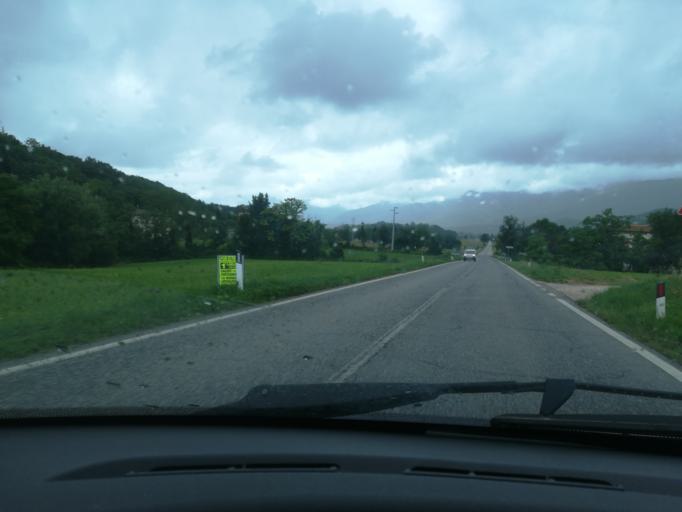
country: IT
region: The Marches
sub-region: Provincia di Macerata
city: Cessapalombo
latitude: 43.0736
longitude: 13.2781
